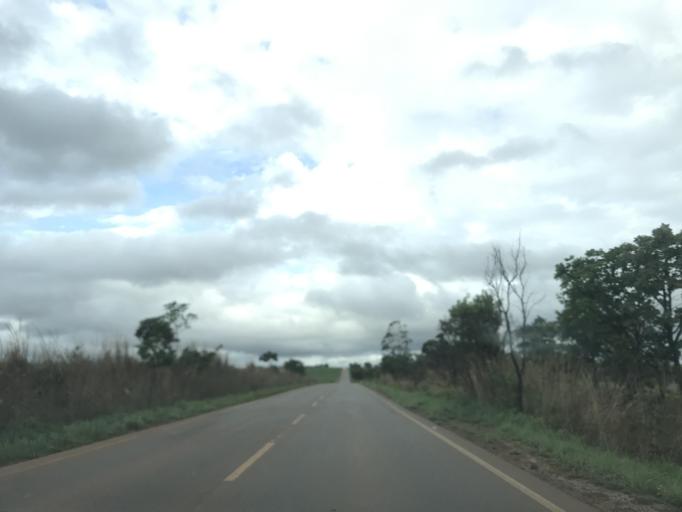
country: BR
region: Goias
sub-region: Vianopolis
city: Vianopolis
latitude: -16.5633
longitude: -48.2868
